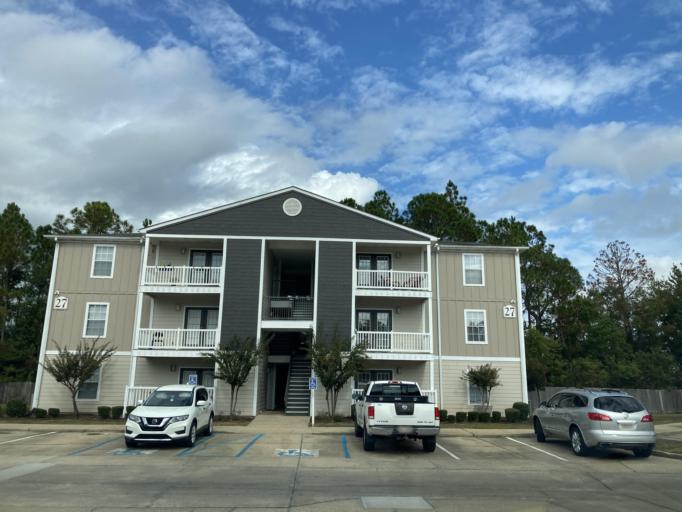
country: US
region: Mississippi
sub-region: Jackson County
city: Gulf Hills
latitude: 30.4367
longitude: -88.8337
